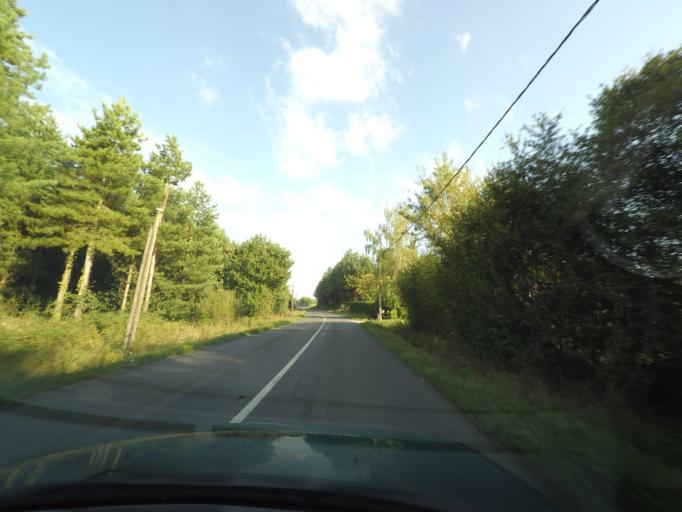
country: FR
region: Pays de la Loire
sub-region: Departement de la Loire-Atlantique
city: Saint-Philbert-de-Grand-Lieu
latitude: 47.0281
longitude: -1.6215
